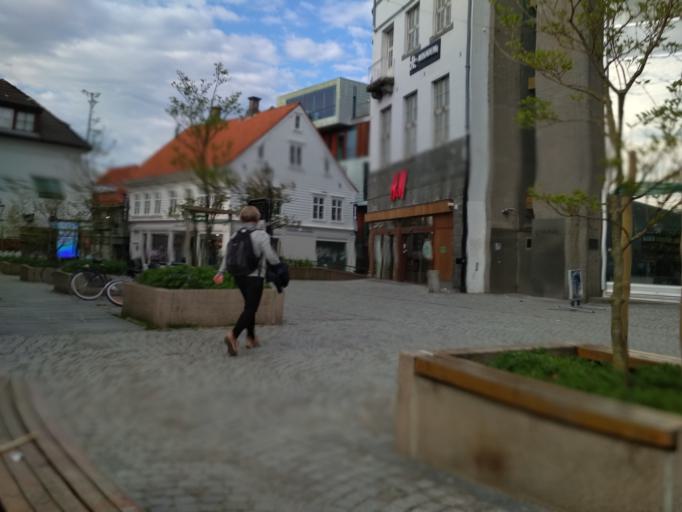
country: NO
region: Rogaland
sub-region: Stavanger
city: Stavanger
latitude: 58.9701
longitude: 5.7334
